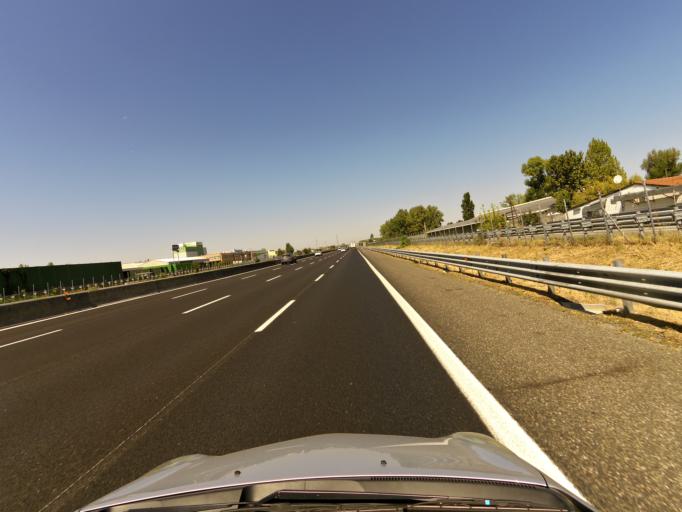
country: IT
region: Emilia-Romagna
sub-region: Provincia di Modena
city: Montale
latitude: 44.6049
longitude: 10.9170
